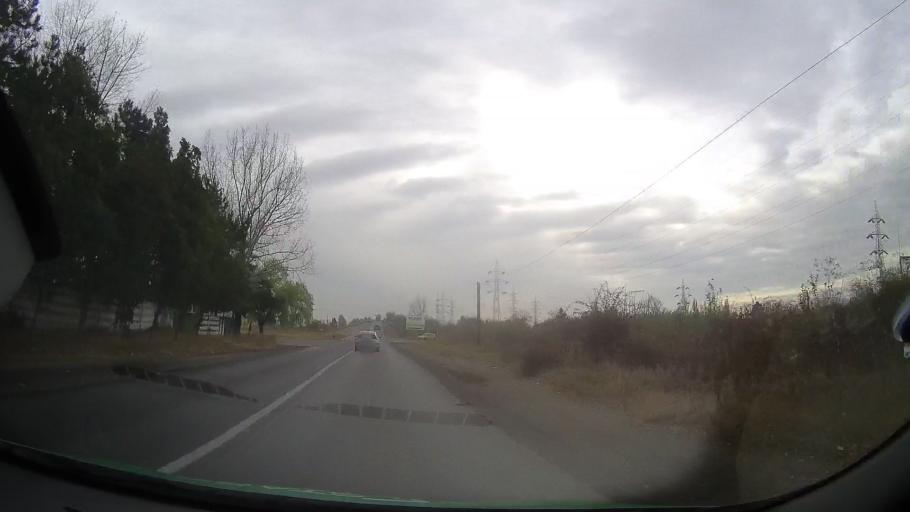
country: RO
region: Prahova
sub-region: Comuna Berceni
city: Berceni
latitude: 44.9434
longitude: 26.1009
